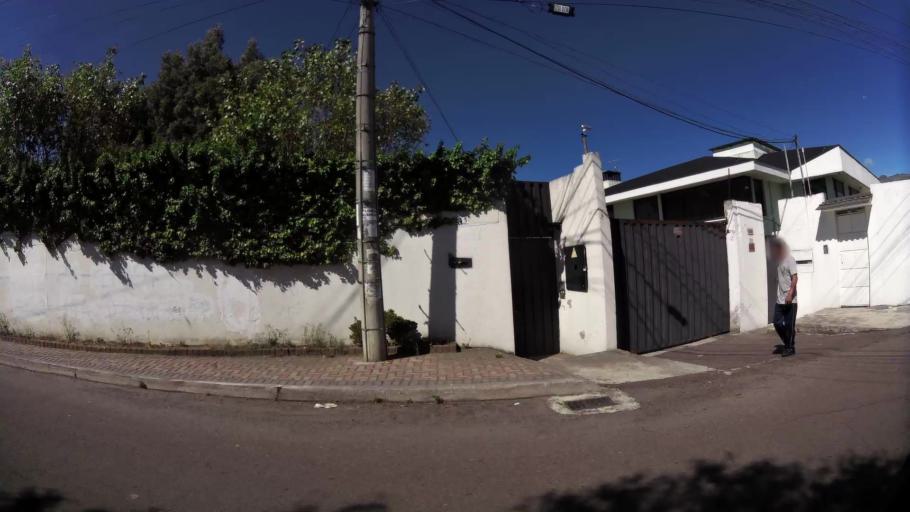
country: EC
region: Pichincha
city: Quito
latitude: -0.1274
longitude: -78.4724
